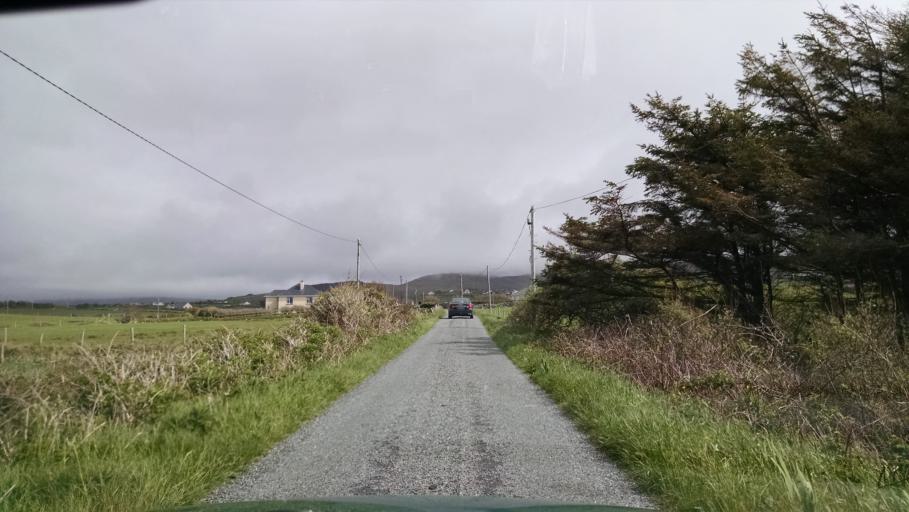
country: IE
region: Connaught
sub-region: County Galway
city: Clifden
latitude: 53.7167
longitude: -9.8911
